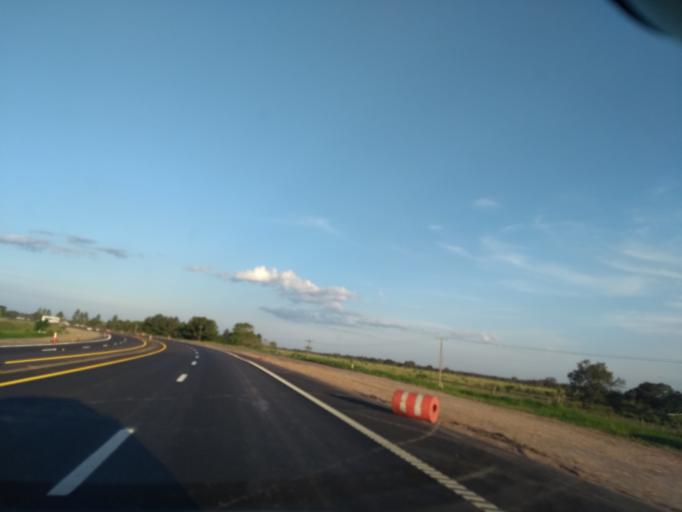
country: AR
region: Chaco
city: Makalle
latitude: -27.1930
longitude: -59.3192
